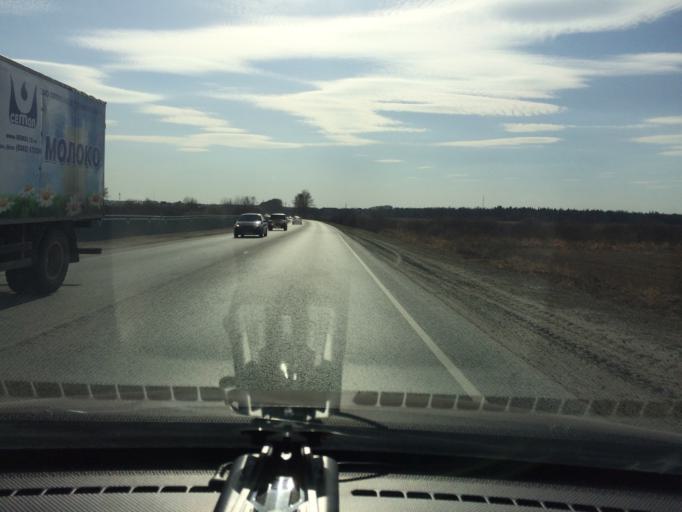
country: RU
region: Mariy-El
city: Yoshkar-Ola
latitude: 56.6561
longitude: 47.9608
